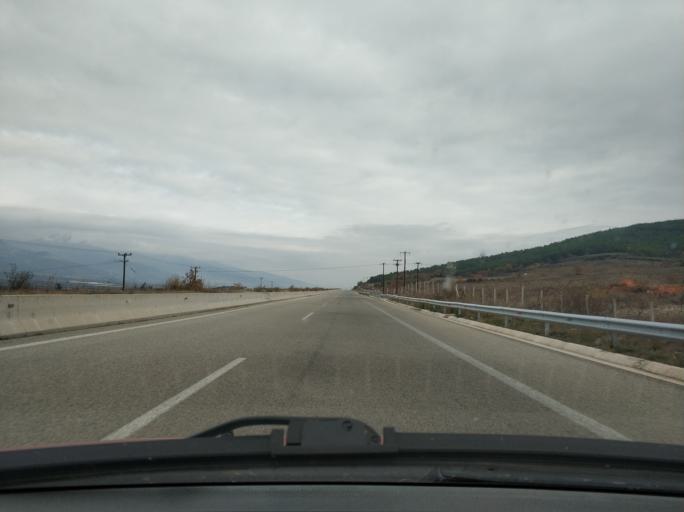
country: GR
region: Central Macedonia
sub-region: Nomos Serron
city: Rodolivos
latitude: 40.8055
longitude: 24.0282
